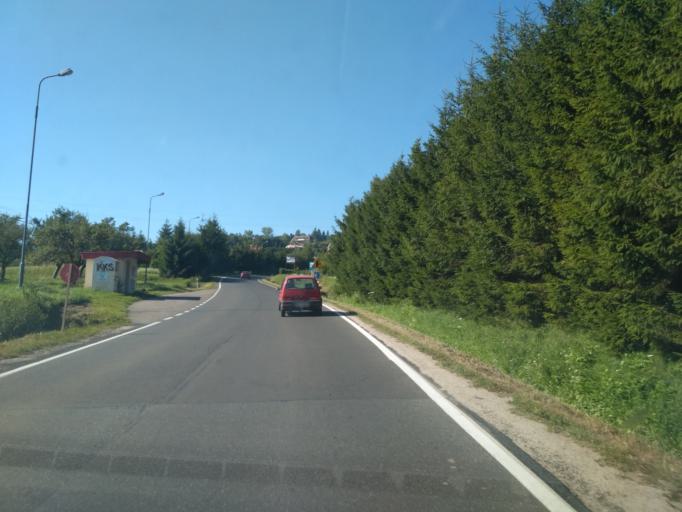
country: PL
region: Subcarpathian Voivodeship
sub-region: Powiat krosnienski
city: Korczyna
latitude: 49.7308
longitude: 21.8094
